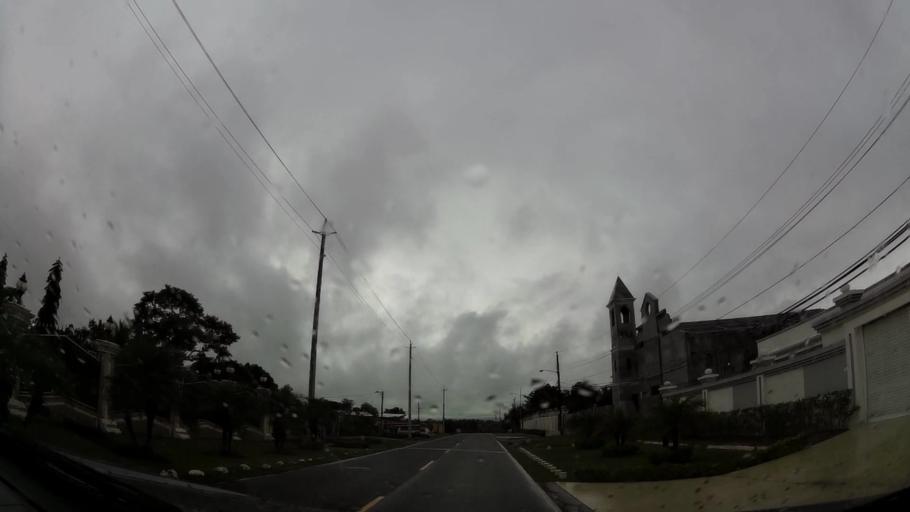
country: PA
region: Veraguas
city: Santiago de Veraguas
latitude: 8.0932
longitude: -80.9593
